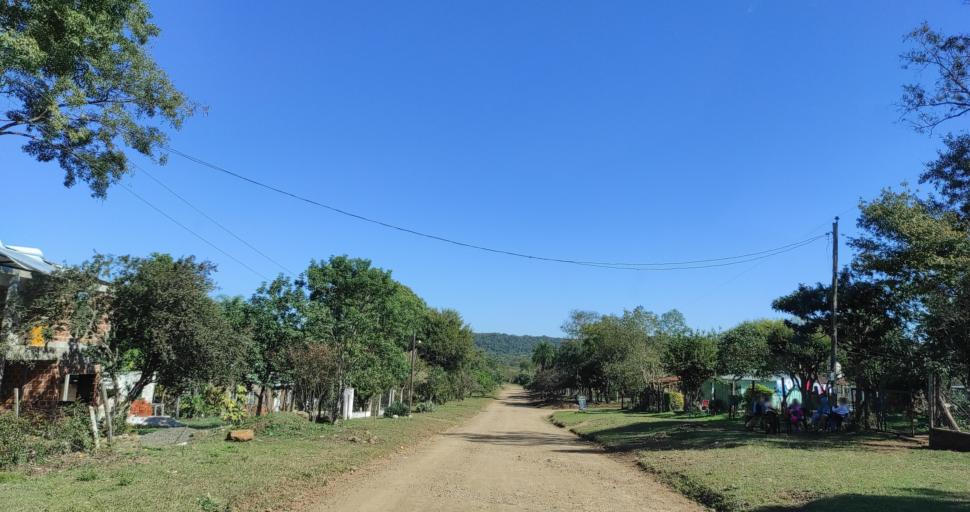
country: AR
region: Misiones
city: Cerro Cora
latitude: -27.5627
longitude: -55.7031
